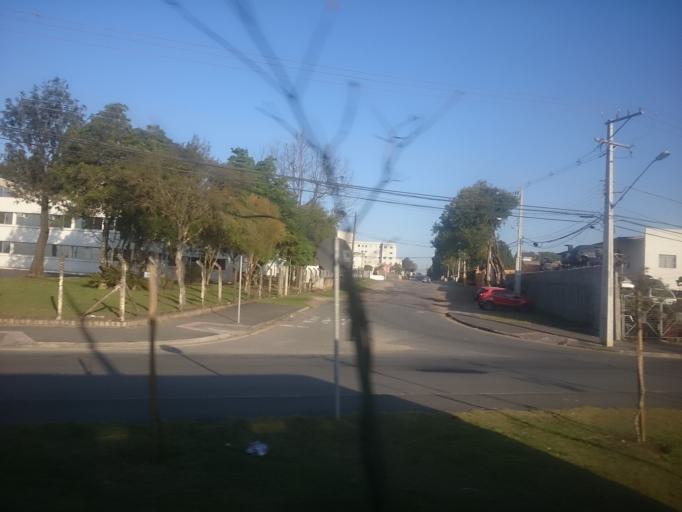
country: BR
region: Parana
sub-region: Curitiba
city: Curitiba
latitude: -25.4808
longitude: -49.2630
